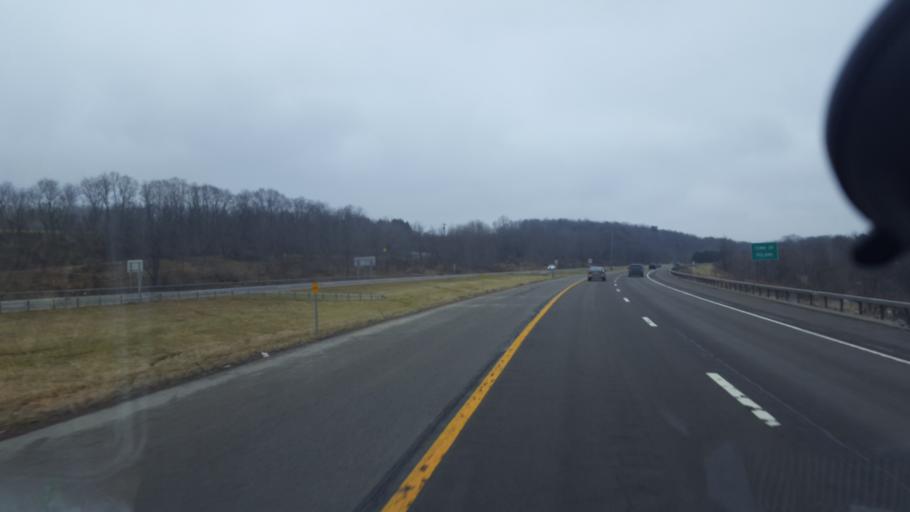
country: US
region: New York
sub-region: Chautauqua County
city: Falconer
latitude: 42.1363
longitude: -79.1795
